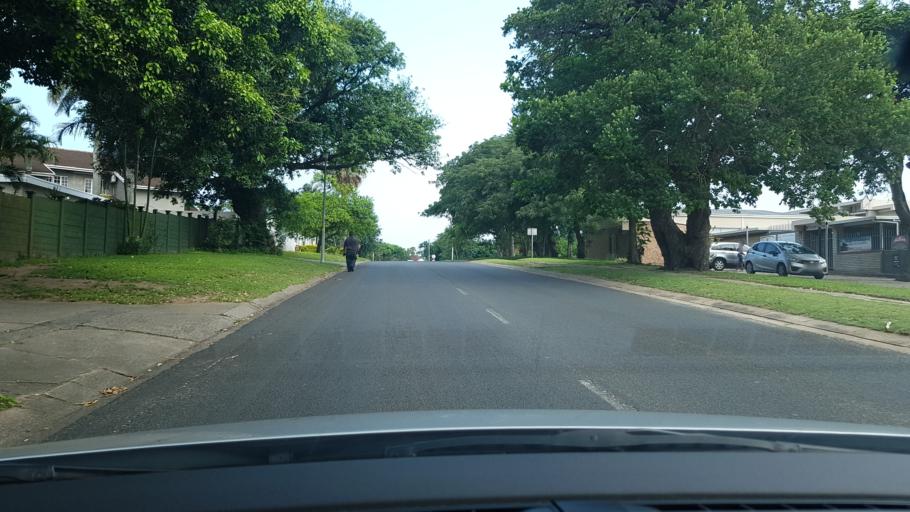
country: ZA
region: KwaZulu-Natal
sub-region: uThungulu District Municipality
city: Richards Bay
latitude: -28.7771
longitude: 32.1002
